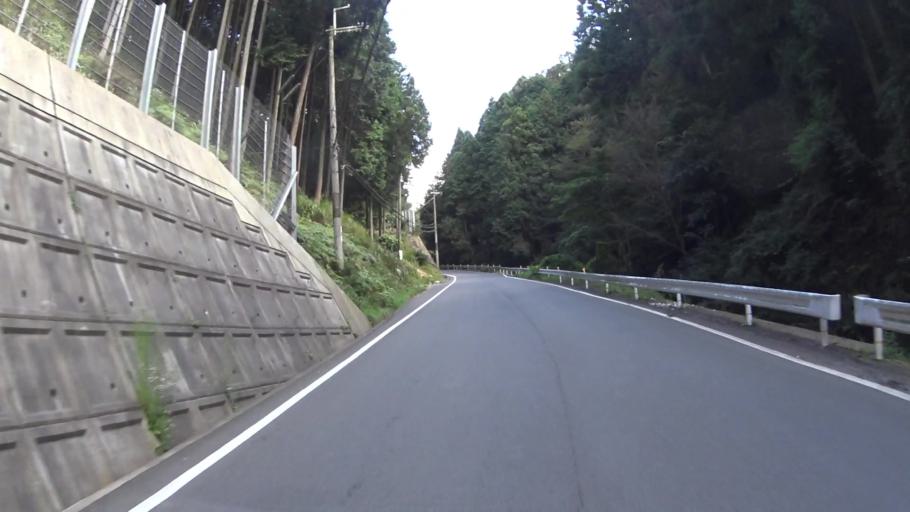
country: JP
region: Kyoto
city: Uji
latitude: 34.9215
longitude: 135.8233
